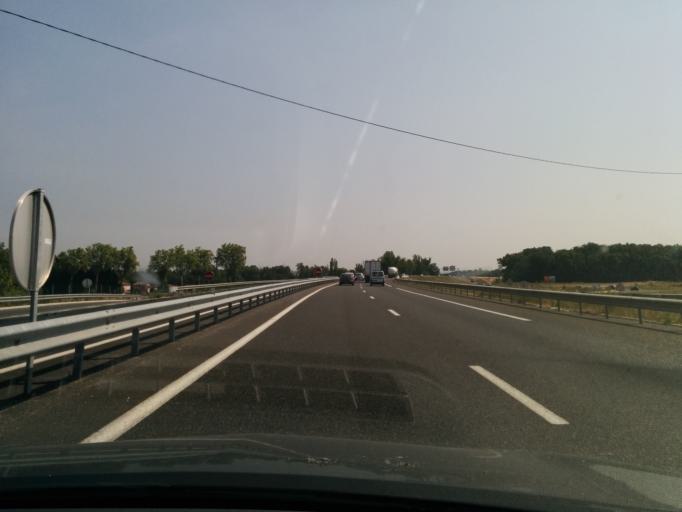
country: FR
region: Midi-Pyrenees
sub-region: Departement du Tarn
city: Marssac-sur-Tarn
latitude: 43.9130
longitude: 2.0527
